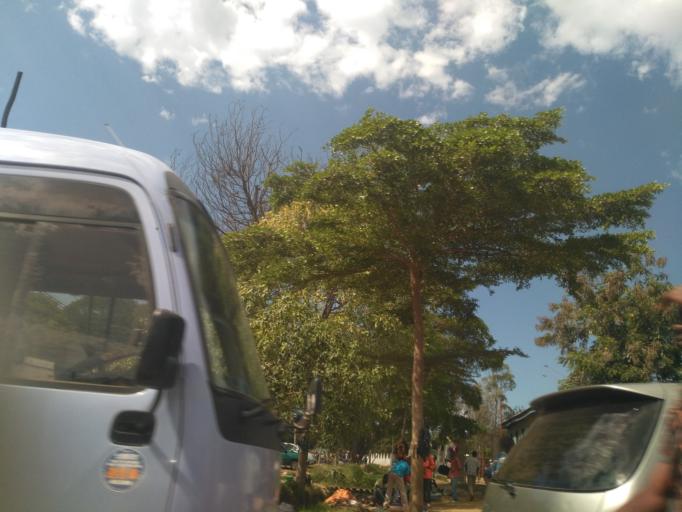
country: TZ
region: Mwanza
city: Mwanza
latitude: -2.5157
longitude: 32.9043
